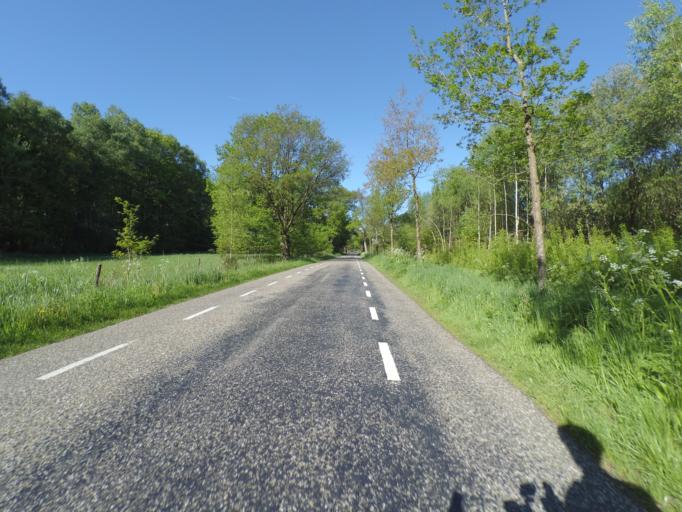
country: NL
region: Gelderland
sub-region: Gemeente Brummen
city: Brummen
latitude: 52.1225
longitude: 6.1124
